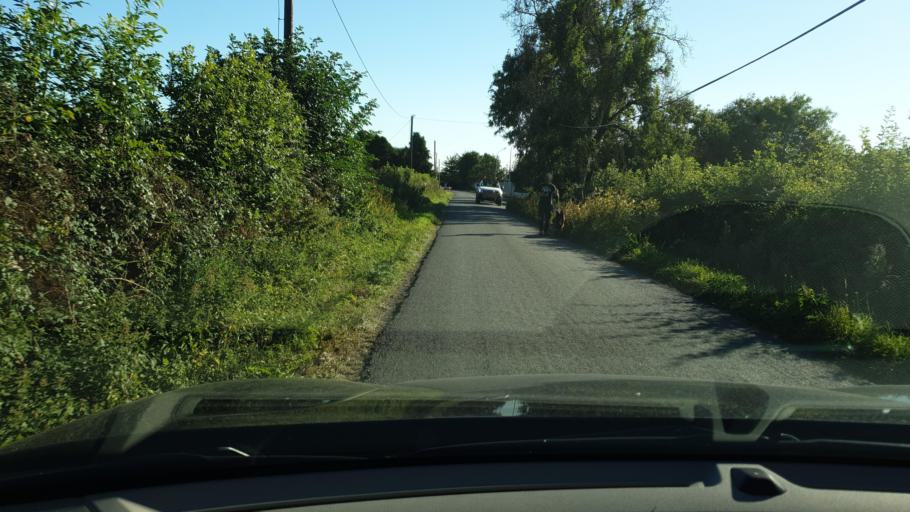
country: IE
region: Leinster
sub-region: An Mhi
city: Ashbourne
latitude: 53.4585
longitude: -6.3676
